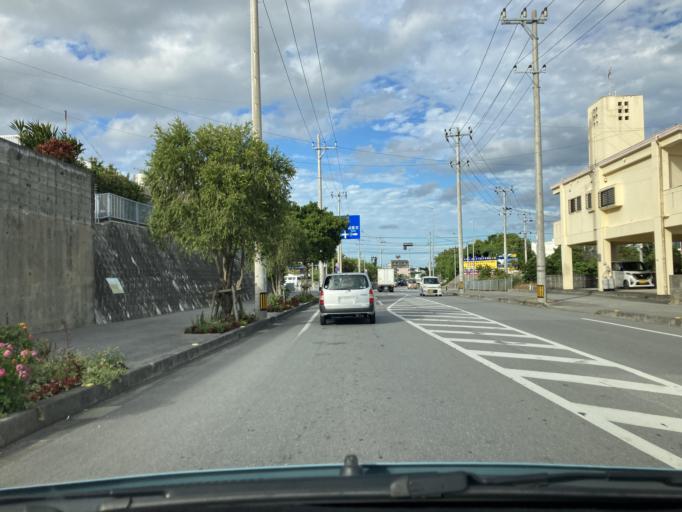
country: JP
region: Okinawa
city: Gushikawa
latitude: 26.3724
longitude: 127.8269
